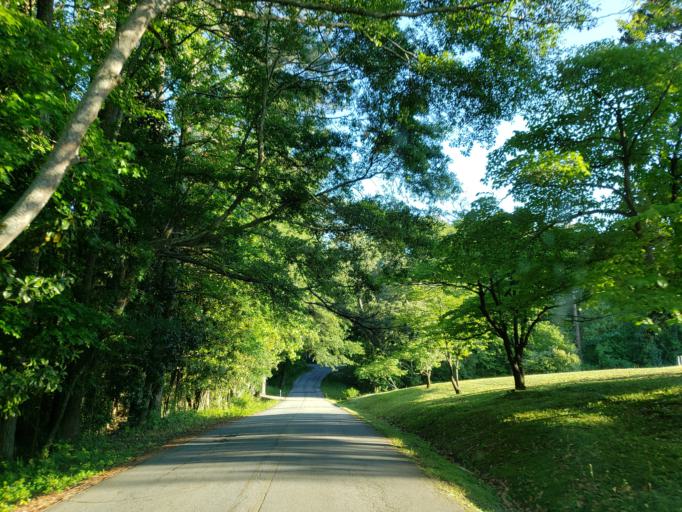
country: US
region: Georgia
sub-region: Haralson County
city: Tallapoosa
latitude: 33.7469
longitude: -85.2950
